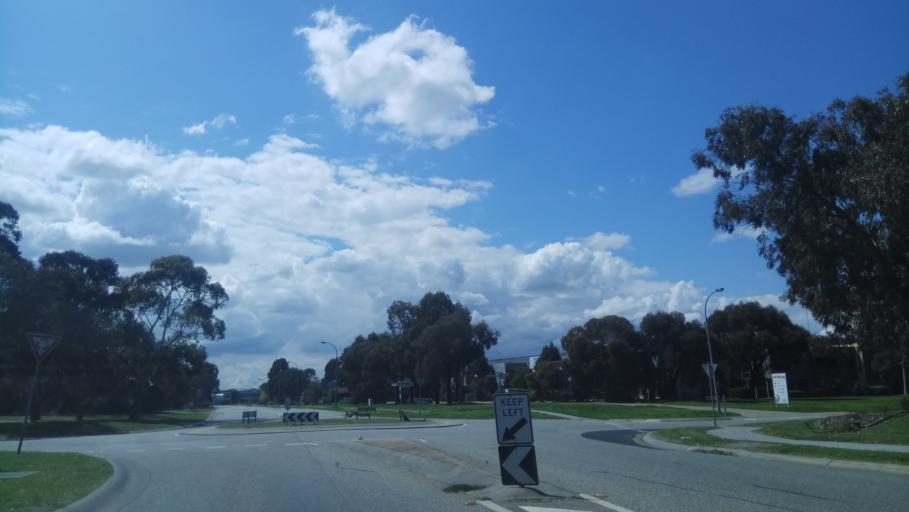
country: AU
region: Victoria
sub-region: Kingston
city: Waterways
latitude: -37.9992
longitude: 145.1189
